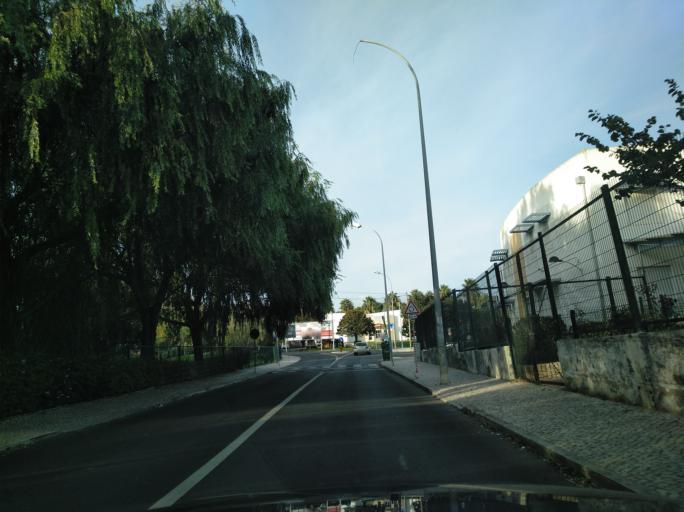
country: PT
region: Lisbon
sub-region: Oeiras
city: Linda-a-Velha
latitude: 38.7227
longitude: -9.2253
